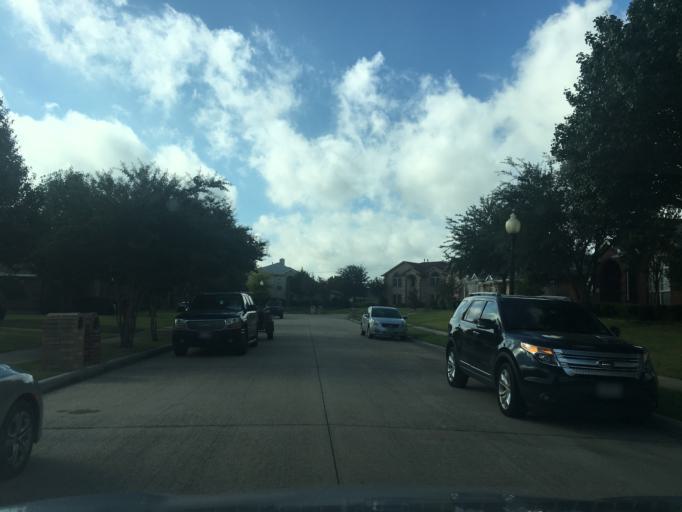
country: US
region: Texas
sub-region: Dallas County
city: Sachse
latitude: 32.9683
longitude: -96.5877
